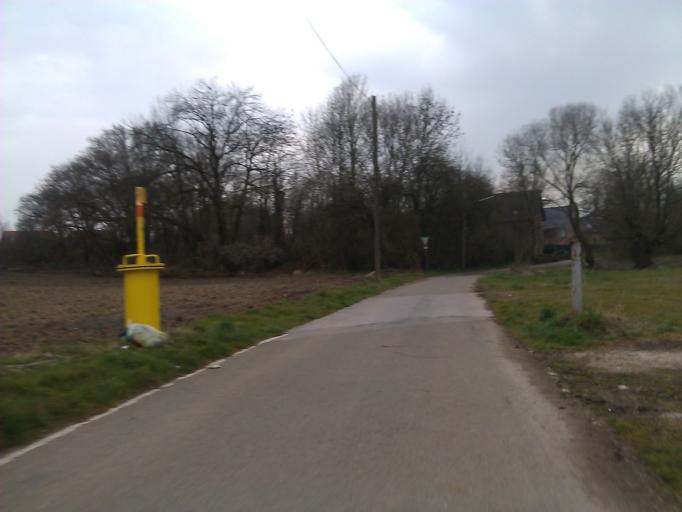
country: DE
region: North Rhine-Westphalia
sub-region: Regierungsbezirk Koln
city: Leverkusen
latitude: 51.0403
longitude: 6.9396
